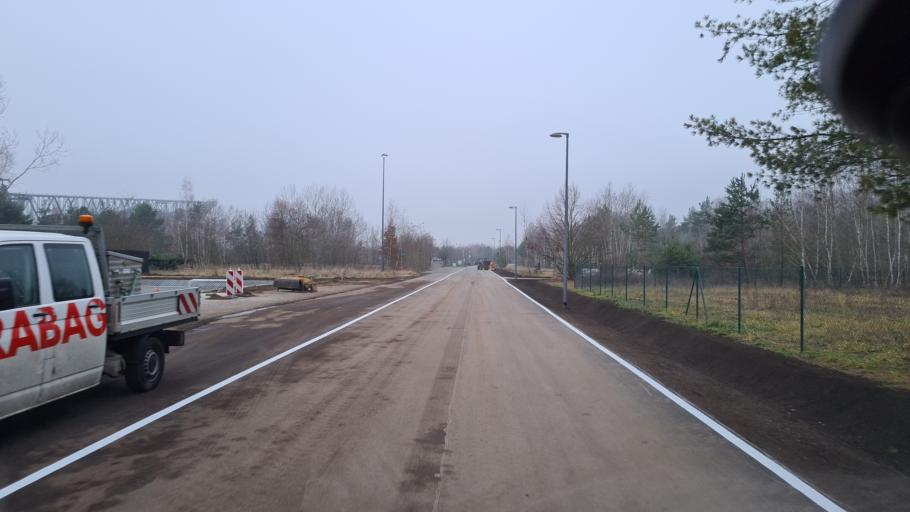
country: DE
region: Brandenburg
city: Sallgast
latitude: 51.5892
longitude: 13.7848
